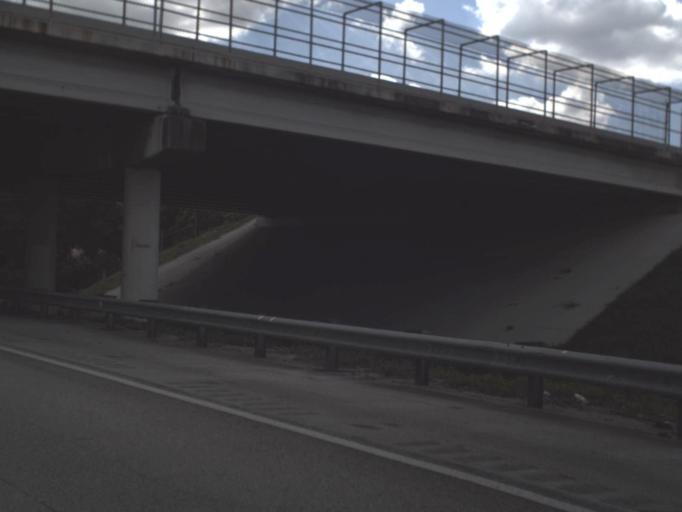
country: US
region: Florida
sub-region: Broward County
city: Miramar
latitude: 25.9822
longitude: -80.2302
